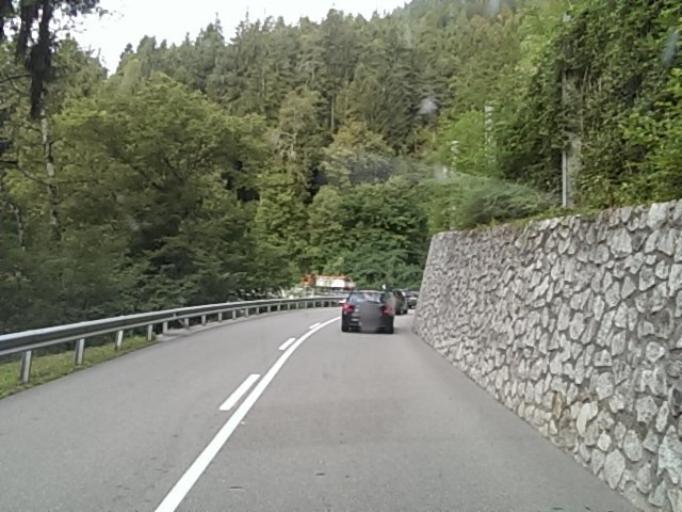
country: IT
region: Trentino-Alto Adige
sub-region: Bolzano
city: San Pancrazio
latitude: 46.6053
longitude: 11.1032
